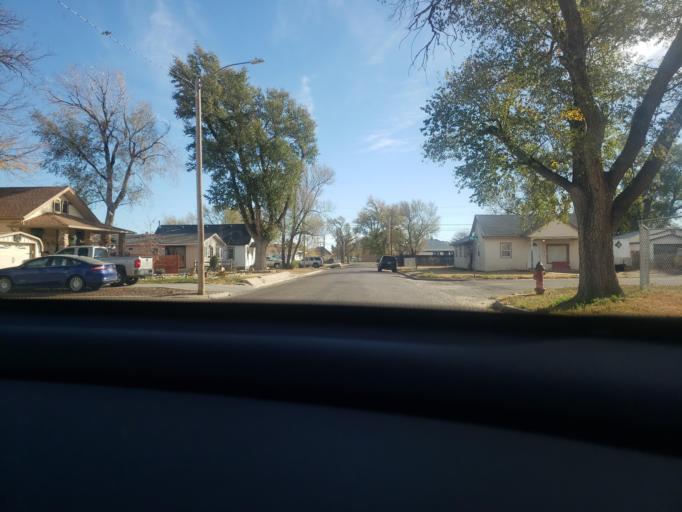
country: US
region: Kansas
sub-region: Finney County
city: Garden City
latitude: 37.9770
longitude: -100.8772
